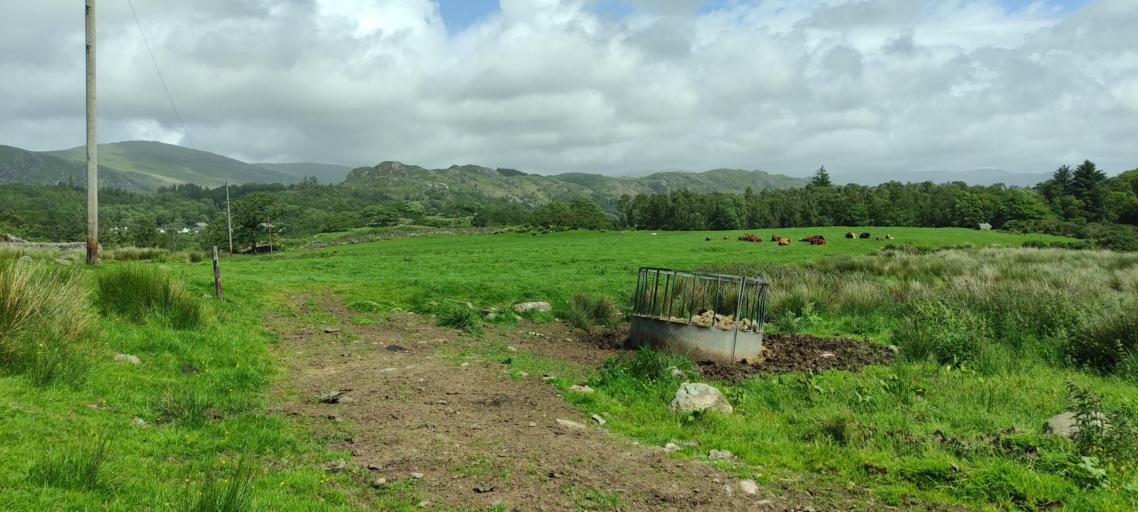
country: GB
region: England
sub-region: Cumbria
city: Seascale
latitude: 54.3815
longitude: -3.3266
